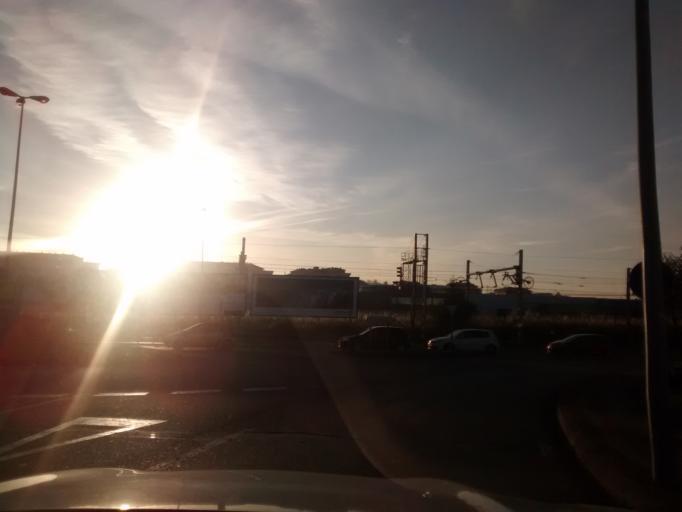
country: ES
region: Cantabria
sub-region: Provincia de Cantabria
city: El Astillero
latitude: 43.4257
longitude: -3.8377
